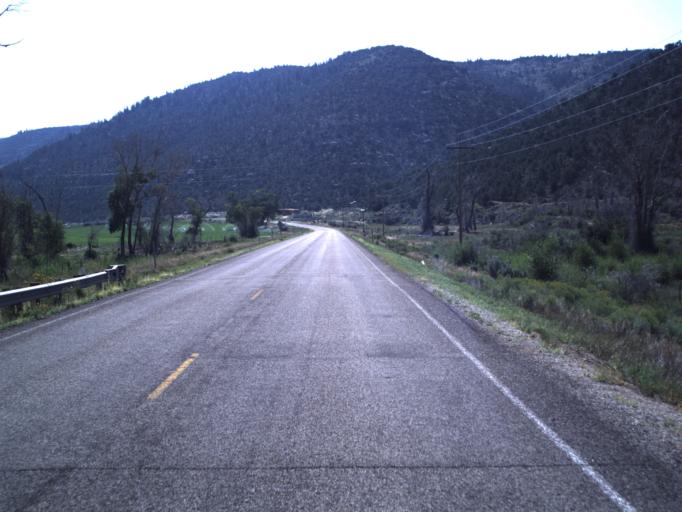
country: US
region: Utah
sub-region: Duchesne County
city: Duchesne
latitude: 40.2996
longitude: -110.6035
